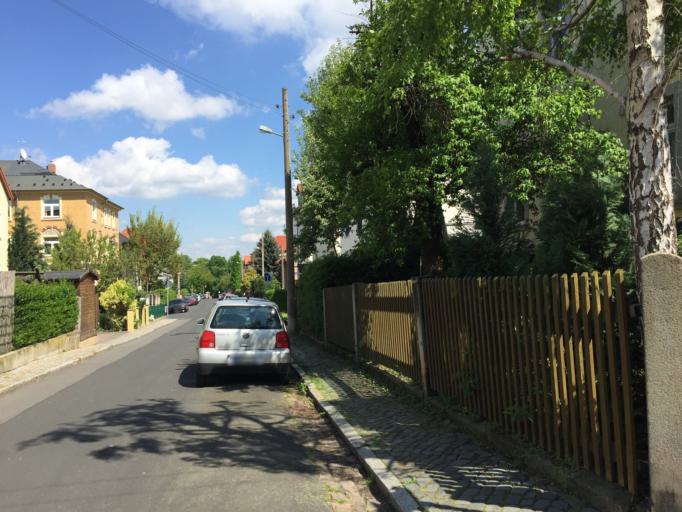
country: DE
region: Saxony
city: Radebeul
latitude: 51.0613
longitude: 13.6690
